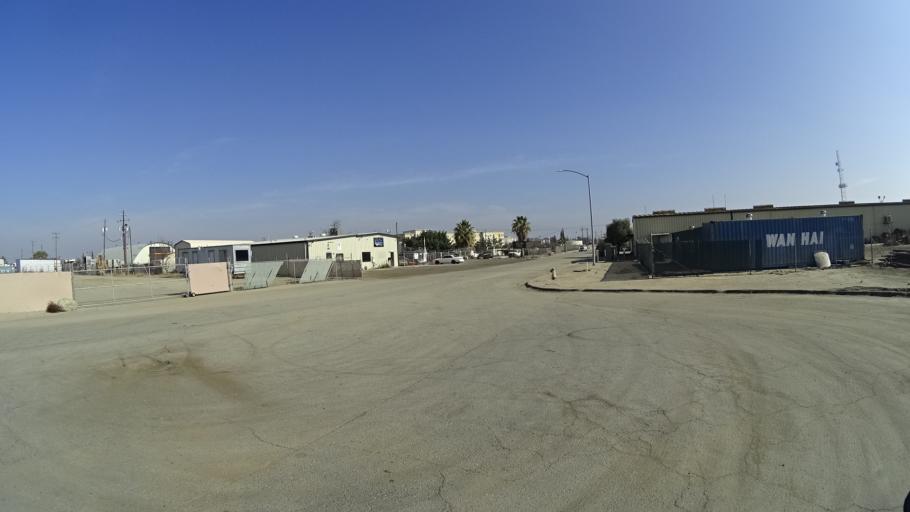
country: US
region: California
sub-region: Kern County
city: Bakersfield
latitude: 35.3786
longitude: -119.0545
